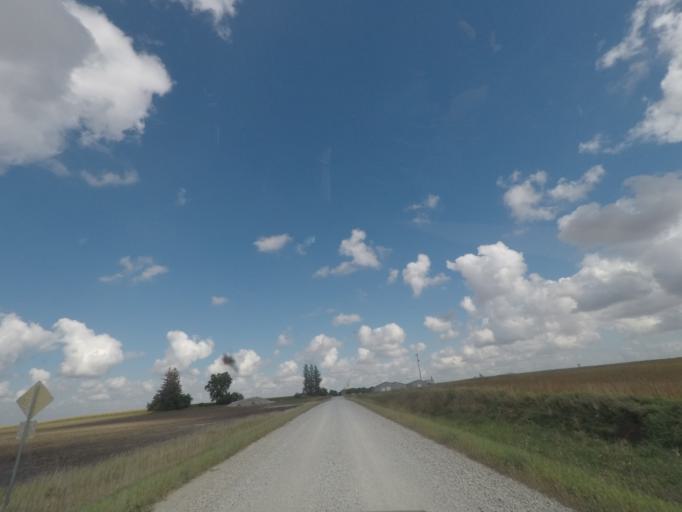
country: US
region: Iowa
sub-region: Story County
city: Nevada
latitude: 42.0023
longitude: -93.3191
